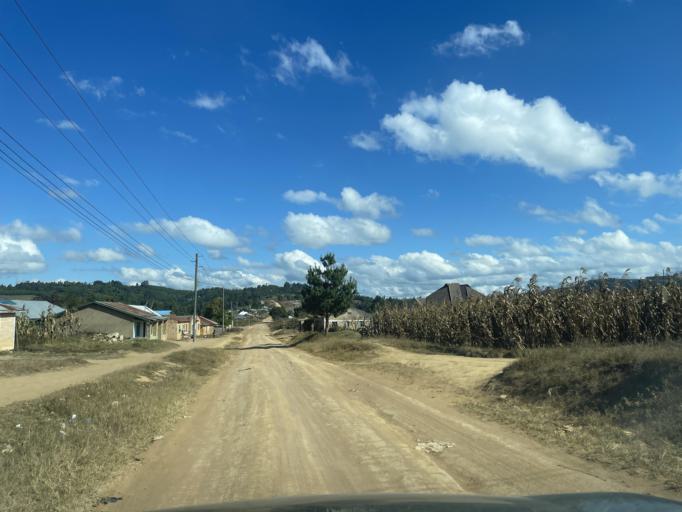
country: TZ
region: Iringa
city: Makungu
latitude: -8.4201
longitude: 35.4197
